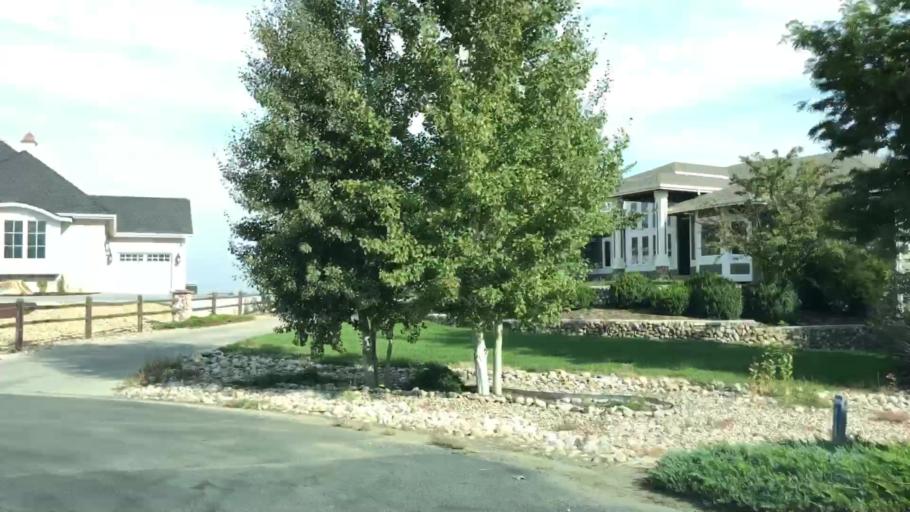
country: US
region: Colorado
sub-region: Larimer County
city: Loveland
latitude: 40.4372
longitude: -105.0515
